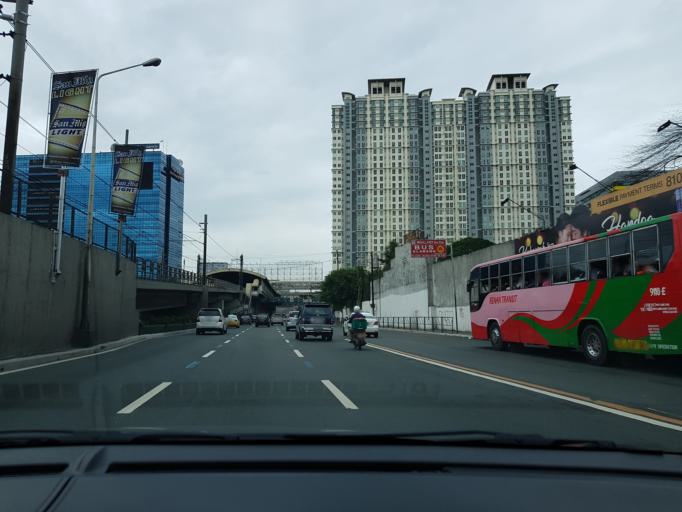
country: PH
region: Metro Manila
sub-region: Makati City
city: Makati City
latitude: 14.5432
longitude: 121.0208
